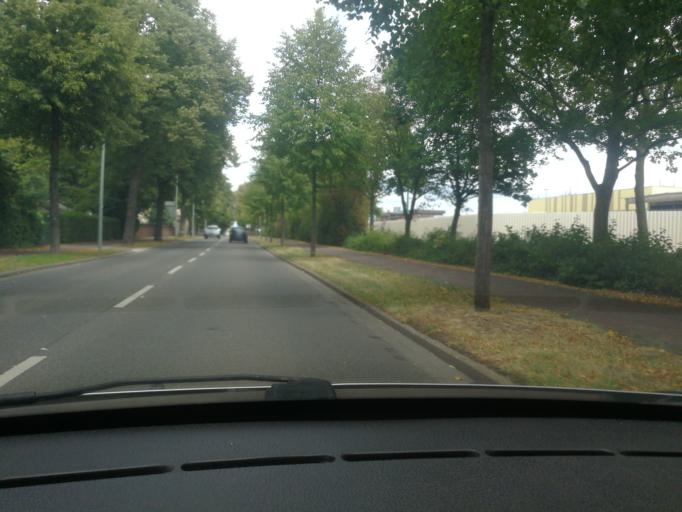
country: DE
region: North Rhine-Westphalia
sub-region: Regierungsbezirk Dusseldorf
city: Krefeld
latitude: 51.3772
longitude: 6.6518
